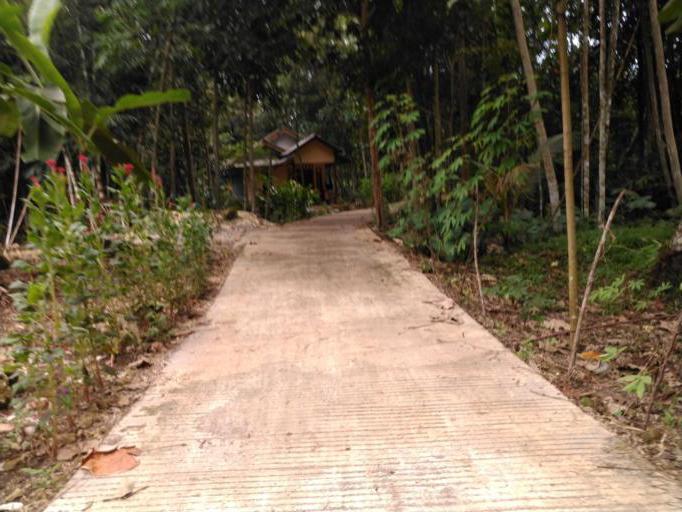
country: ID
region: West Java
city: Cigugur
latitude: -7.6435
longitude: 108.4218
